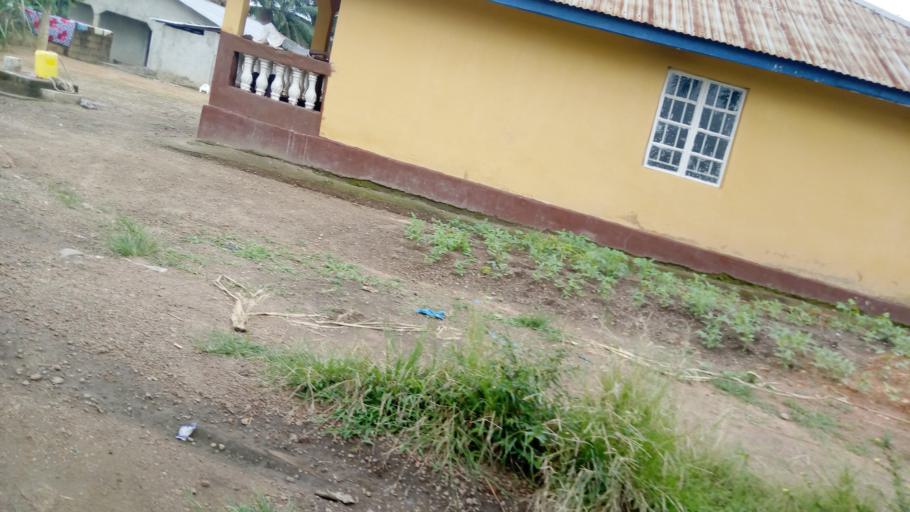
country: SL
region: Northern Province
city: Makeni
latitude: 8.8918
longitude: -12.0287
